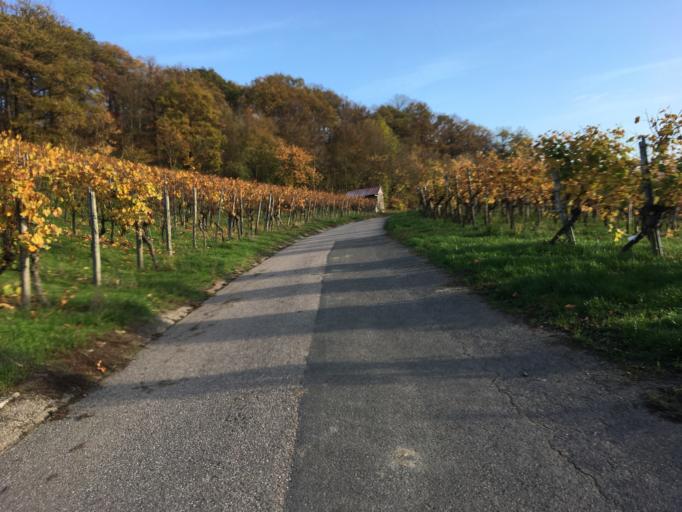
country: DE
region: Baden-Wuerttemberg
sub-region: Regierungsbezirk Stuttgart
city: Erlenbach
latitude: 49.1481
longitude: 9.2537
